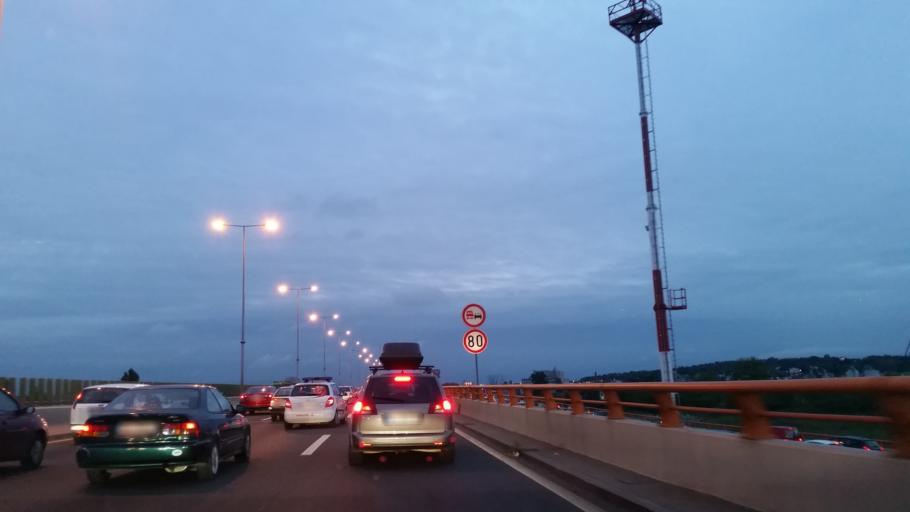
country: RS
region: Central Serbia
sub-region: Belgrade
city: Novi Beograd
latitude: 44.8056
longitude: 20.4346
